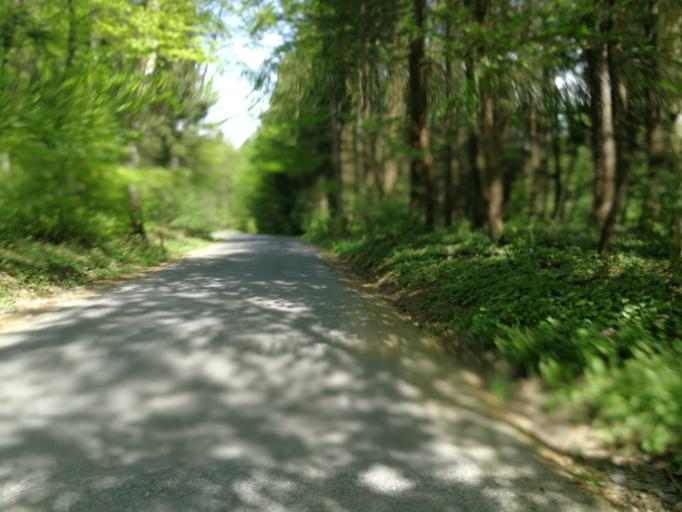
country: CH
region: Zurich
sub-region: Bezirk Hinwil
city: Binzikon
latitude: 47.2871
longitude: 8.7558
